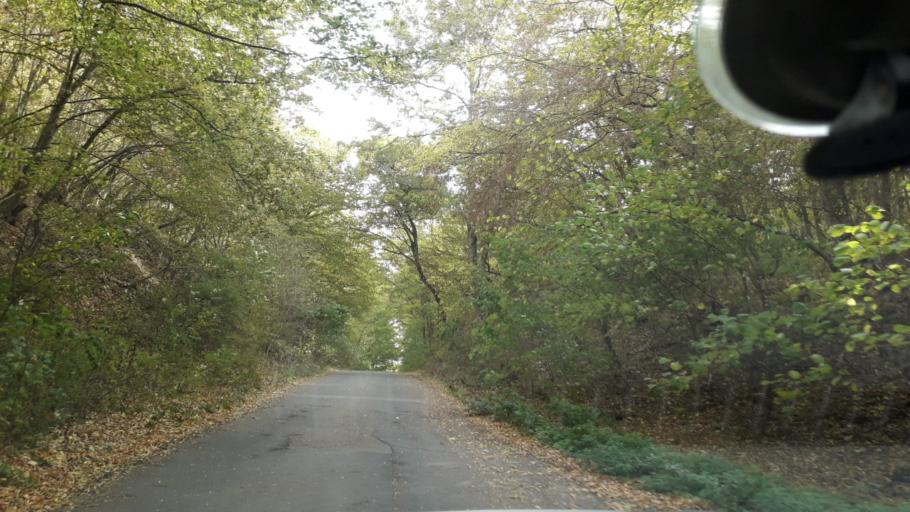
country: DE
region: Lower Saxony
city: Liebenburg
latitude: 52.0002
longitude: 10.4275
